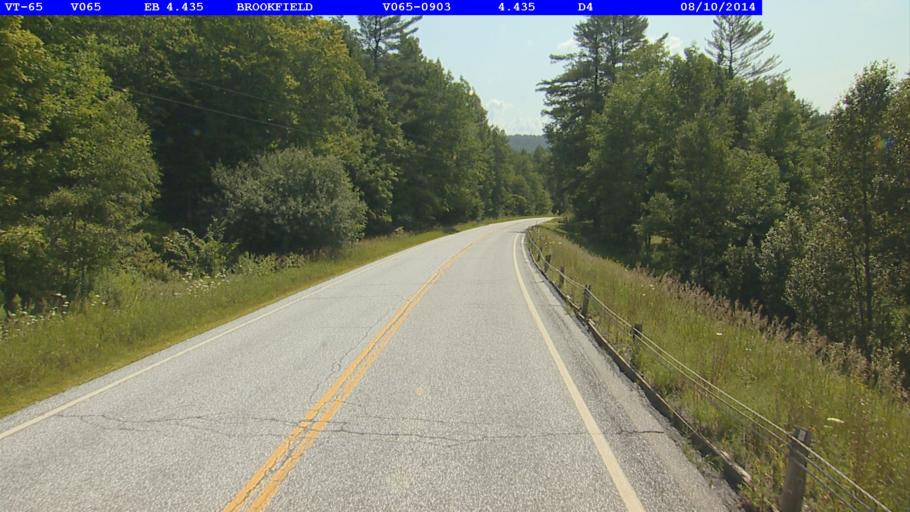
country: US
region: Vermont
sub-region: Orange County
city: Williamstown
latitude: 44.0300
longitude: -72.5839
